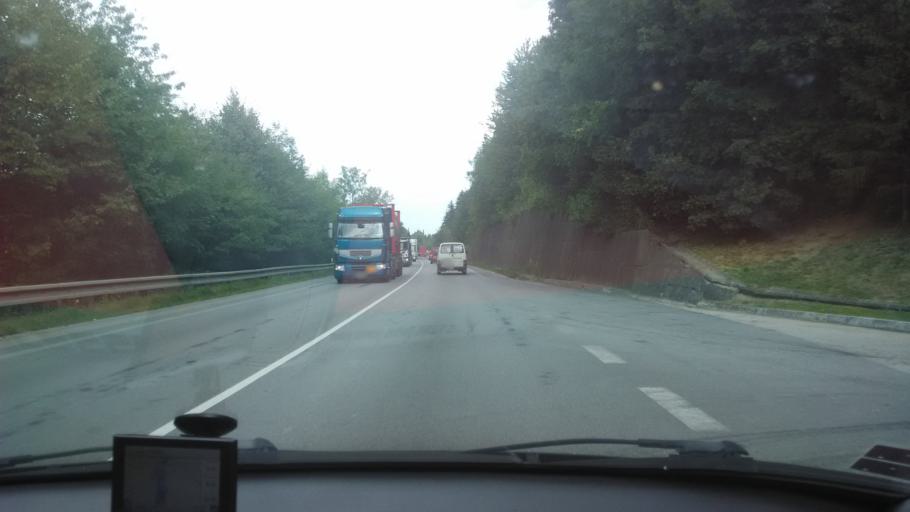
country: SK
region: Zilinsky
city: Kysucke Nove Mesto
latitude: 49.2896
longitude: 18.7813
